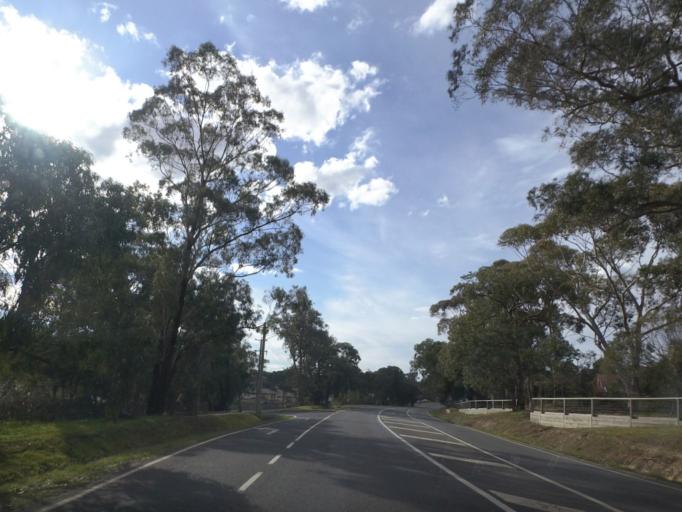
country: AU
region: Victoria
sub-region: Manningham
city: Donvale
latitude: -37.7578
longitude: 145.1735
